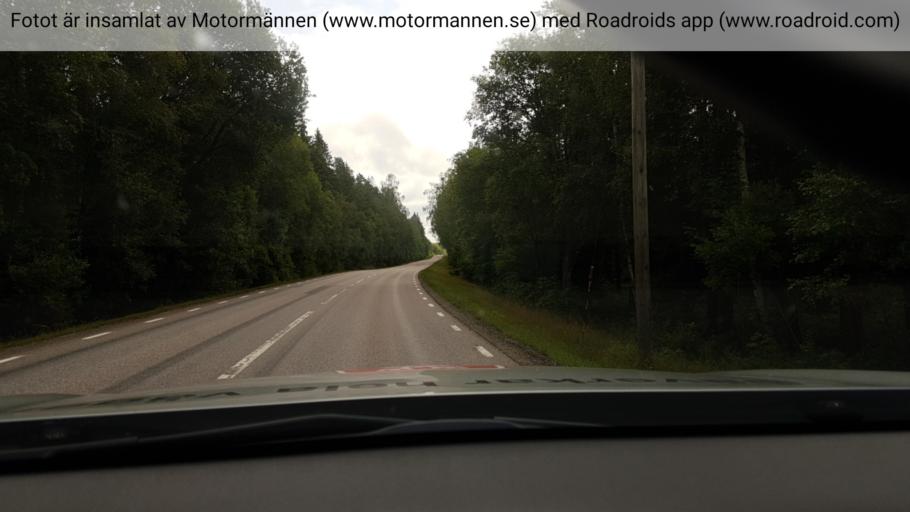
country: SE
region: Vaestra Goetaland
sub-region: Svenljunga Kommun
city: Svenljunga
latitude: 57.4905
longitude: 12.9792
